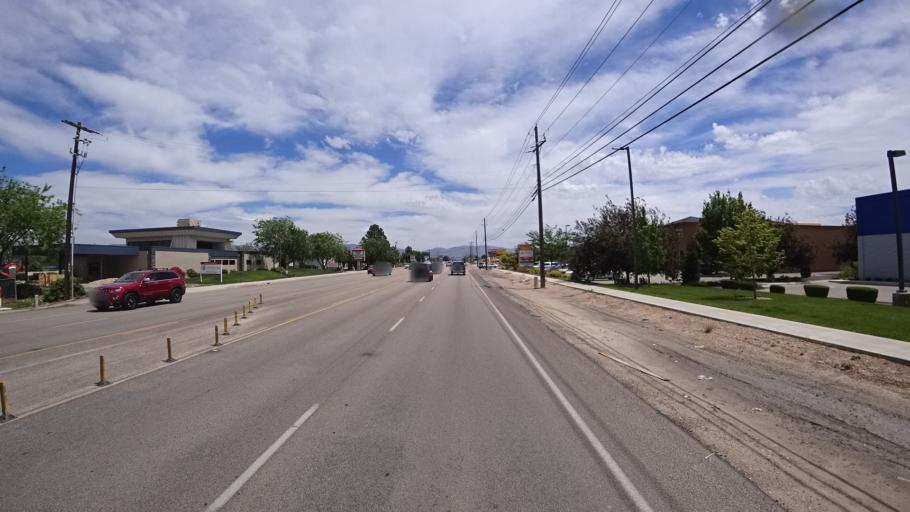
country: US
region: Idaho
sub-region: Ada County
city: Meridian
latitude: 43.6194
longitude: -116.3196
